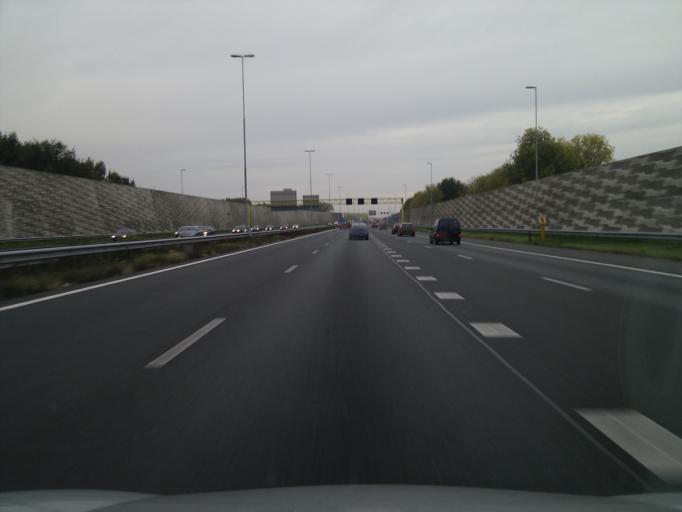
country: NL
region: North Brabant
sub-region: Gemeente 's-Hertogenbosch
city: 's-Hertogenbosch
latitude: 51.7315
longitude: 5.3131
